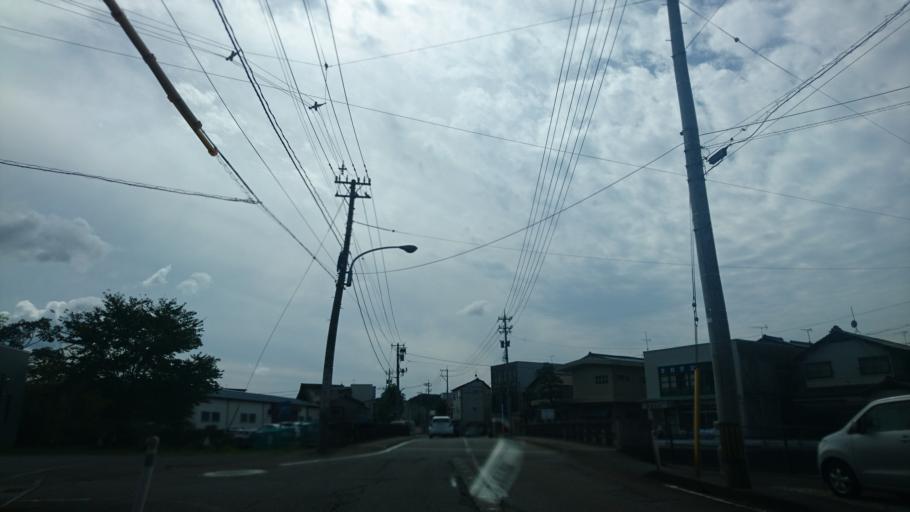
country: JP
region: Fukui
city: Maruoka
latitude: 36.3076
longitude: 136.3154
